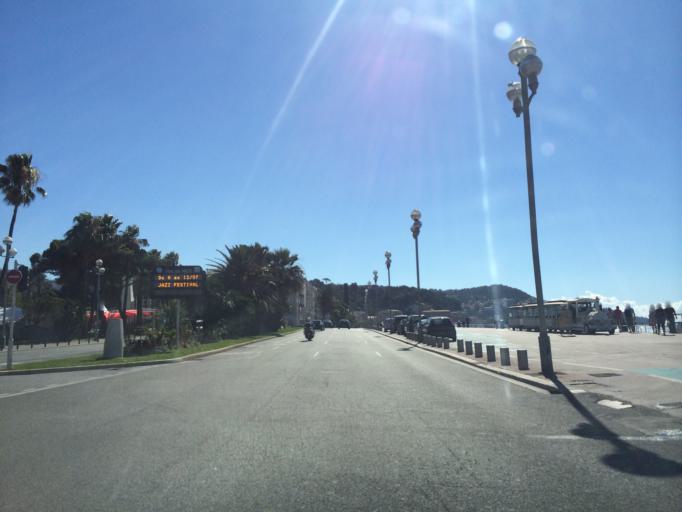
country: FR
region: Provence-Alpes-Cote d'Azur
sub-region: Departement des Alpes-Maritimes
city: Nice
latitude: 43.6949
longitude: 7.2662
